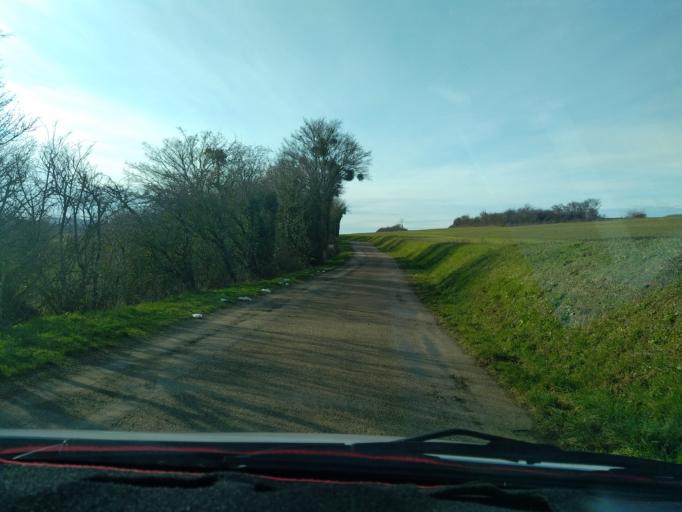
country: FR
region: Franche-Comte
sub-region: Departement de la Haute-Saone
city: Marnay
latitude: 47.3126
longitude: 5.6782
